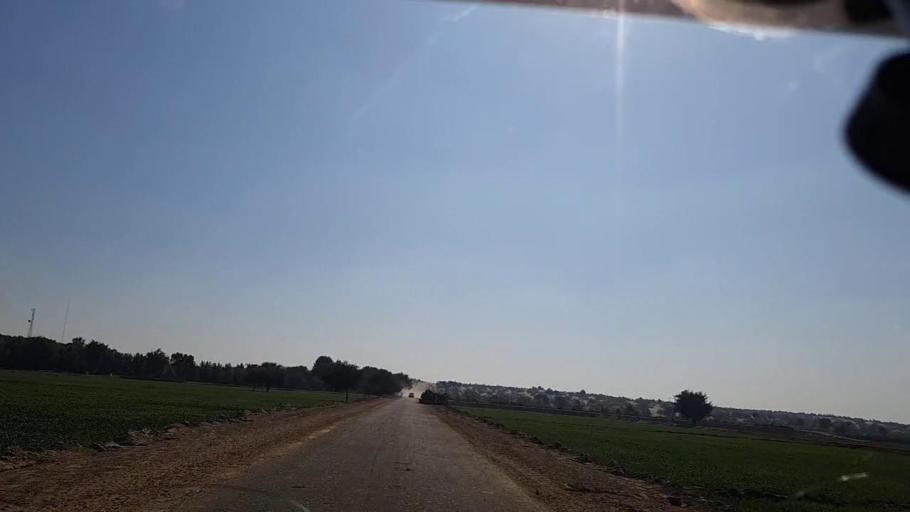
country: PK
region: Sindh
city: Khanpur
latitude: 27.5682
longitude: 69.3888
